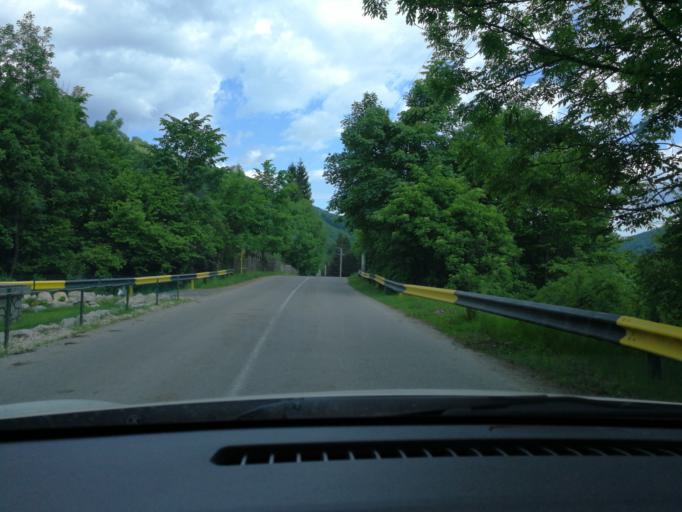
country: RO
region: Prahova
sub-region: Comuna Valea Doftanei
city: Tesila
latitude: 45.2809
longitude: 25.7267
